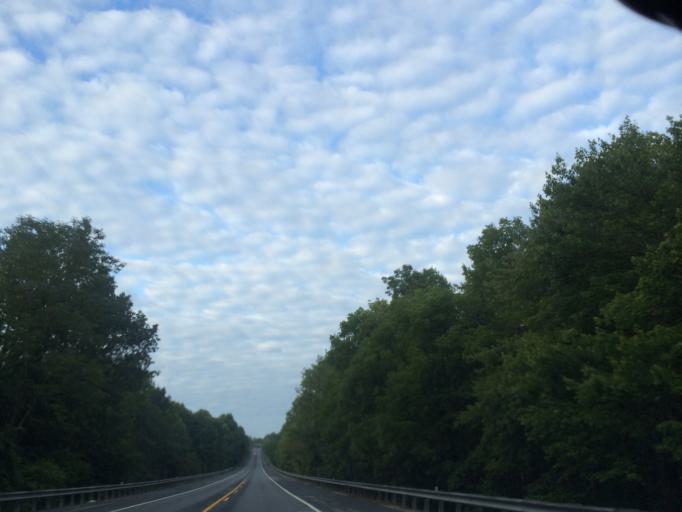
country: US
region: Maryland
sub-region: Carroll County
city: Eldersburg
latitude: 39.4410
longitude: -76.9988
